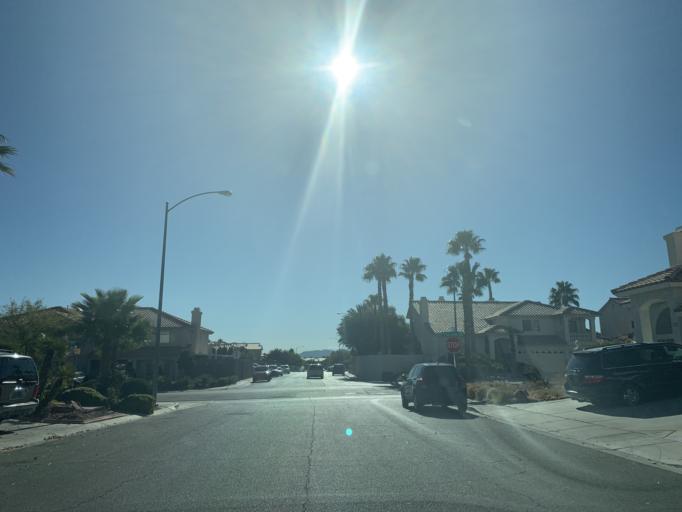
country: US
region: Nevada
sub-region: Clark County
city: Summerlin South
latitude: 36.1212
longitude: -115.2903
